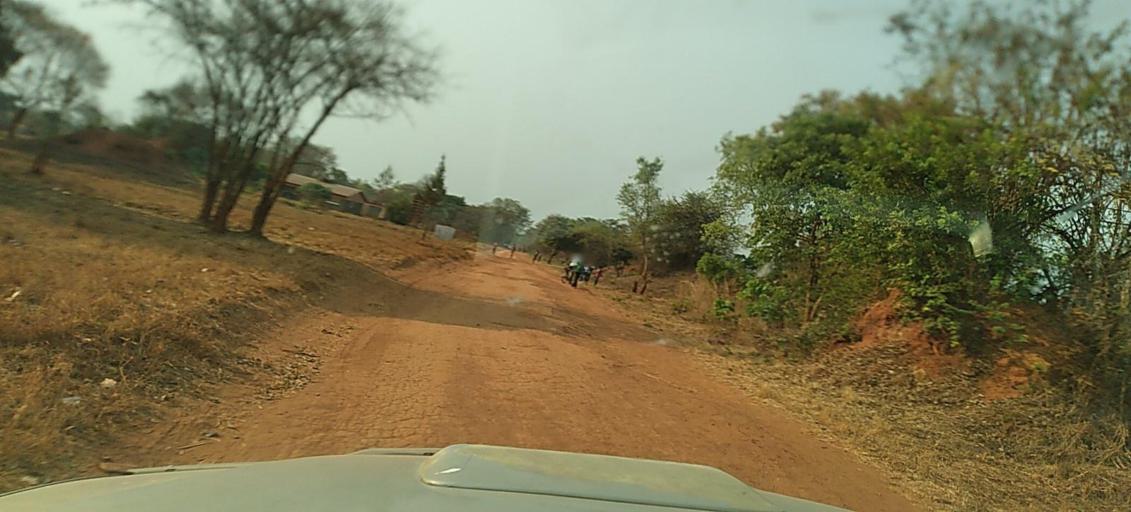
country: ZM
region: North-Western
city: Kasempa
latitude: -13.3013
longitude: 26.5539
